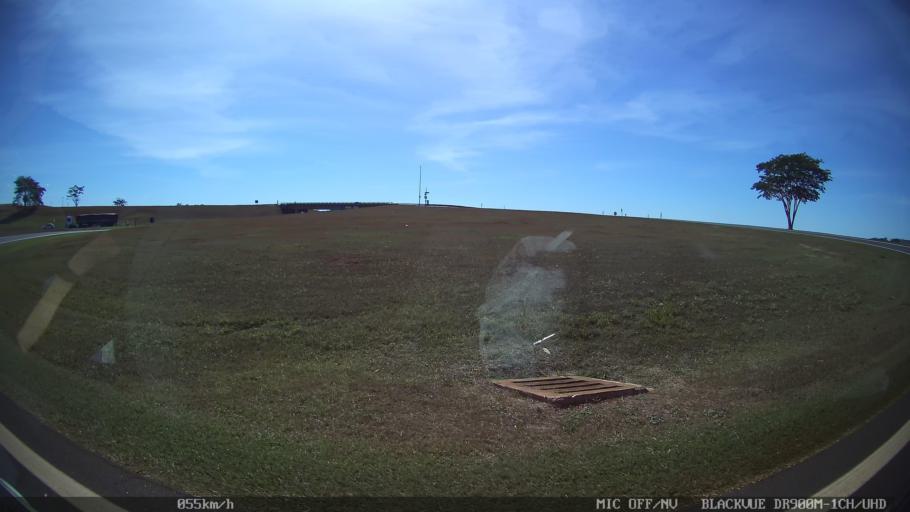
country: BR
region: Sao Paulo
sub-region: Sao Joaquim Da Barra
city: Sao Joaquim da Barra
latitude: -20.5256
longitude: -47.8400
